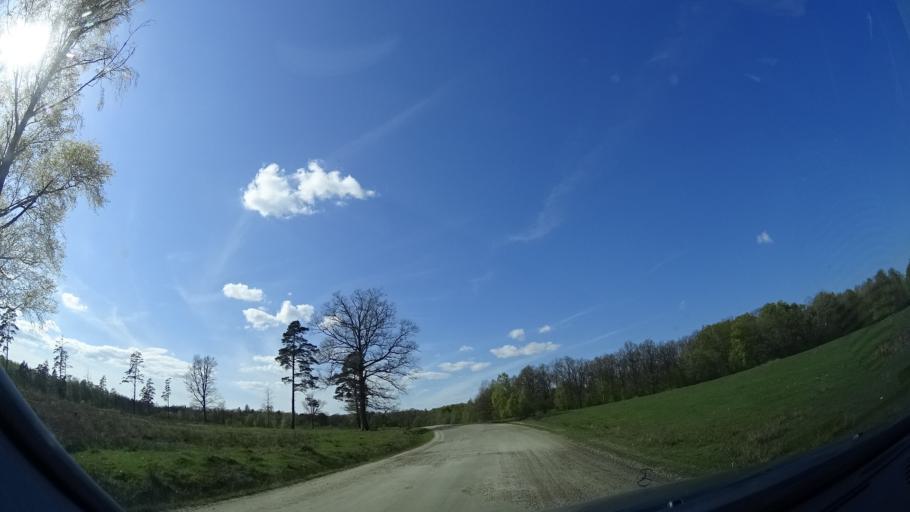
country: SE
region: Skane
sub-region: Hassleholms Kommun
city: Tormestorp
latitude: 56.1107
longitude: 13.6948
